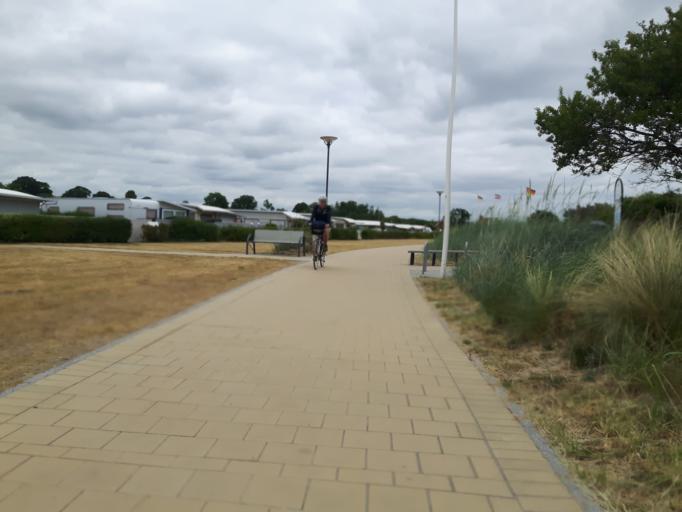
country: DE
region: Schleswig-Holstein
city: Schashagen
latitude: 54.0973
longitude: 10.8925
